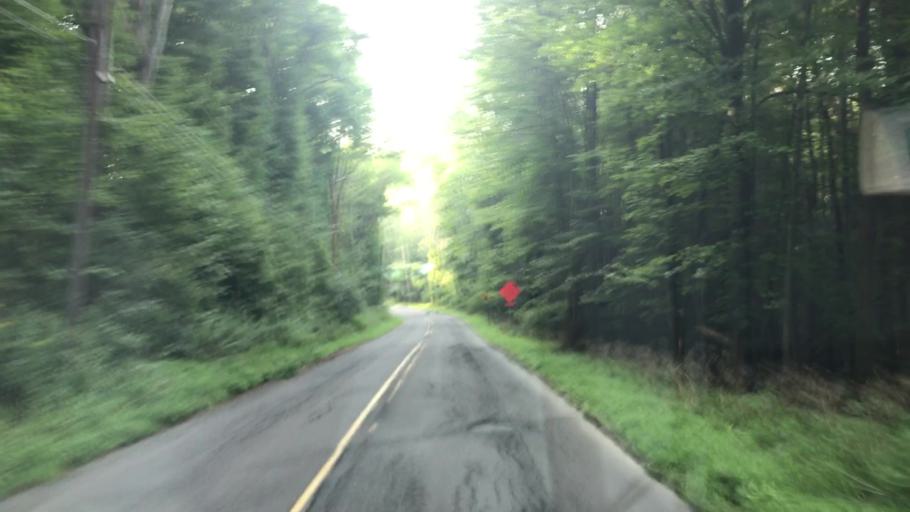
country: US
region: Pennsylvania
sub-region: Wyoming County
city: Factoryville
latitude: 41.6067
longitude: -75.7300
